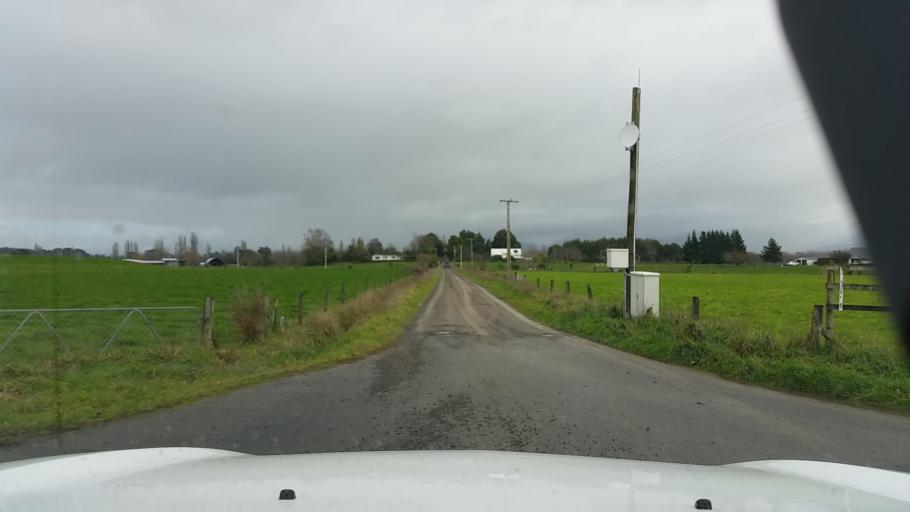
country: NZ
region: Wellington
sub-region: Masterton District
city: Masterton
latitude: -41.0745
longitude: 175.5160
